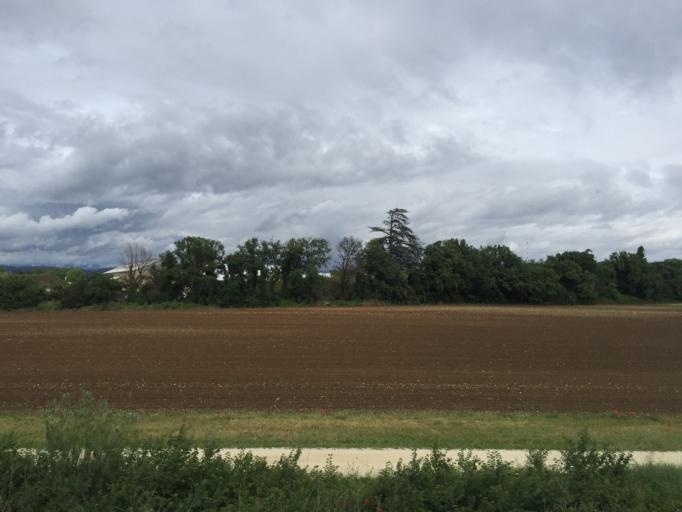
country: FR
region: Rhone-Alpes
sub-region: Departement de la Drome
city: Pierrelatte
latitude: 44.3567
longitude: 4.7014
